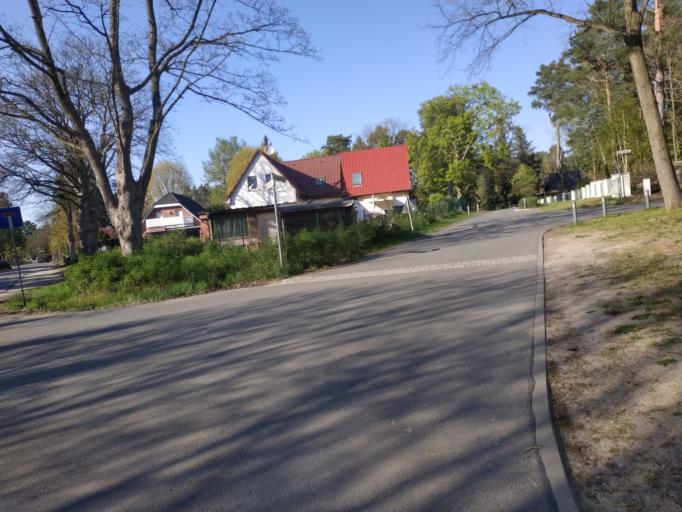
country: DE
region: Brandenburg
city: Petershagen
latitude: 52.5511
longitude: 13.8248
